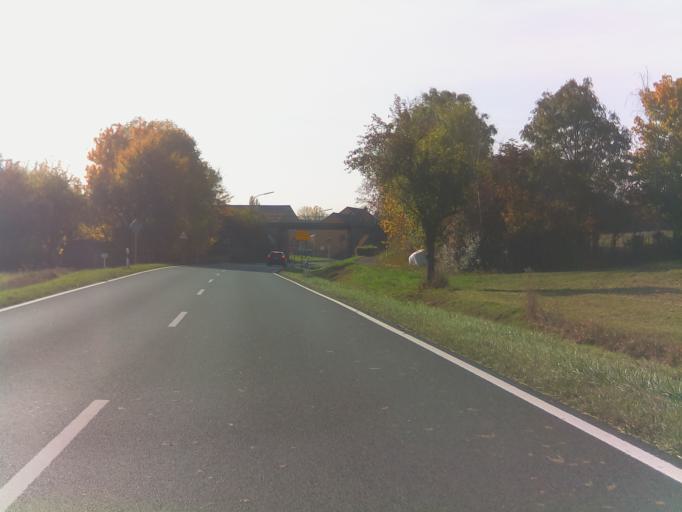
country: DE
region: Bavaria
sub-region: Regierungsbezirk Unterfranken
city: Prichsenstadt
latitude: 49.8388
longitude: 10.3364
